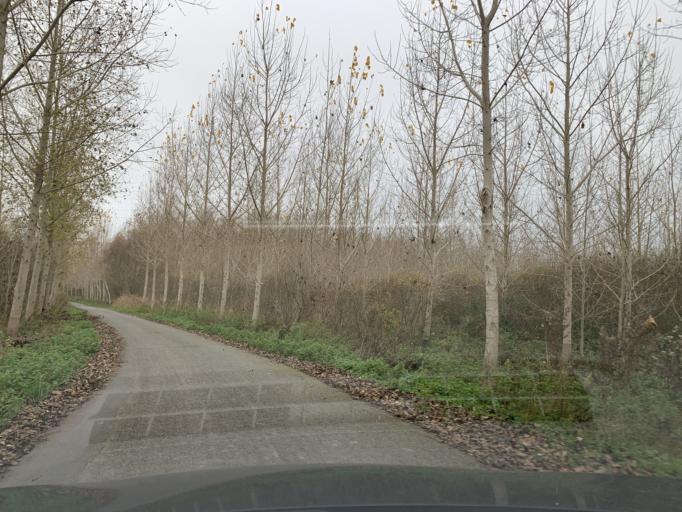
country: FR
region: Nord-Pas-de-Calais
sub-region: Departement du Pas-de-Calais
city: Ecourt-Saint-Quentin
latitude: 50.2516
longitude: 3.0974
